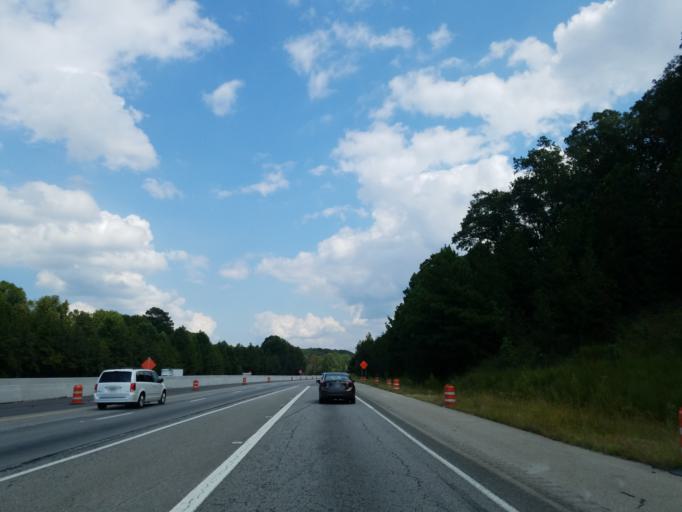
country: US
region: Georgia
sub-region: Gwinnett County
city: Buford
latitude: 34.0573
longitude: -83.9830
